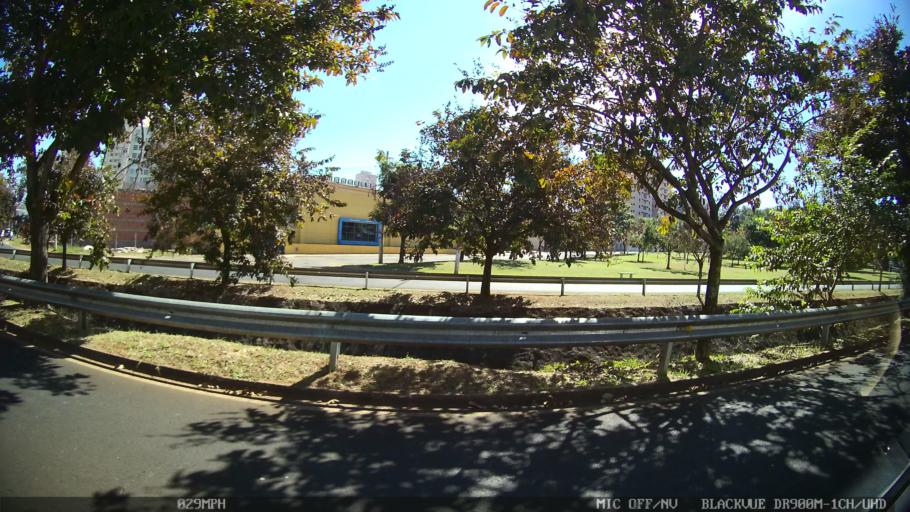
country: BR
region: Sao Paulo
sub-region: Franca
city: Franca
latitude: -20.5516
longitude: -47.4023
